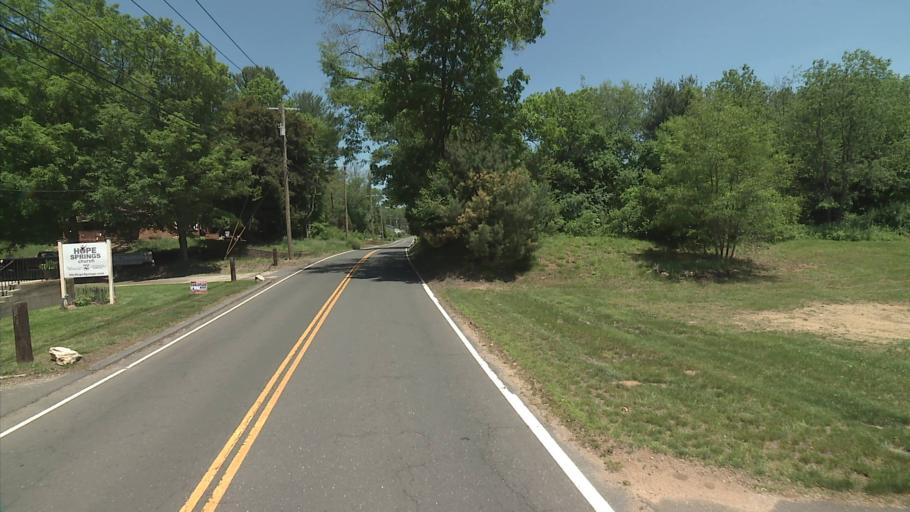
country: US
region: Connecticut
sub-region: Tolland County
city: Stafford Springs
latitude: 41.9649
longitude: -72.2949
